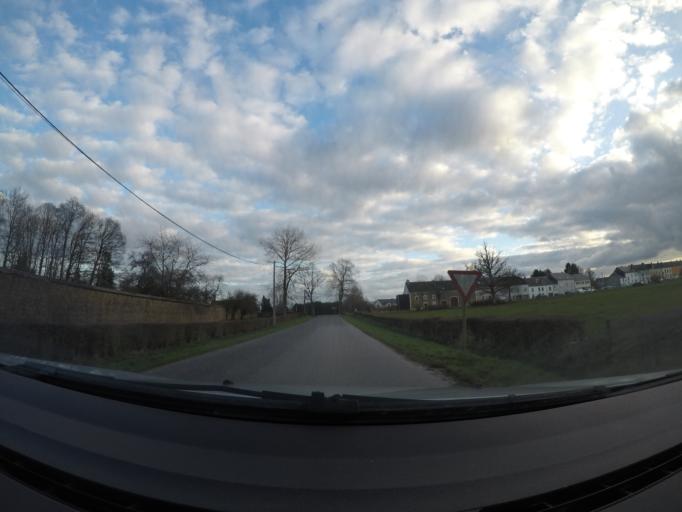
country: BE
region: Wallonia
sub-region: Province du Luxembourg
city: Etalle
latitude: 49.6756
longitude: 5.5653
